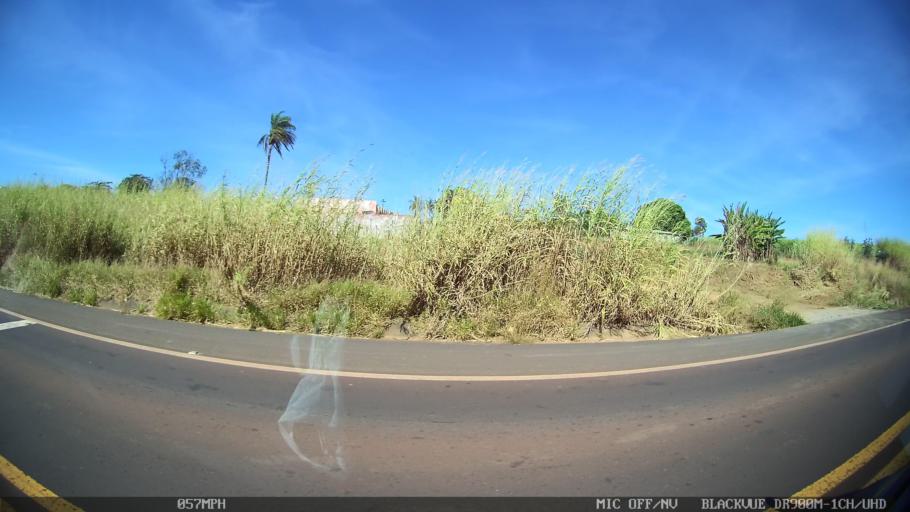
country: BR
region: Sao Paulo
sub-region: Franca
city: Franca
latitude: -20.5598
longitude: -47.5039
